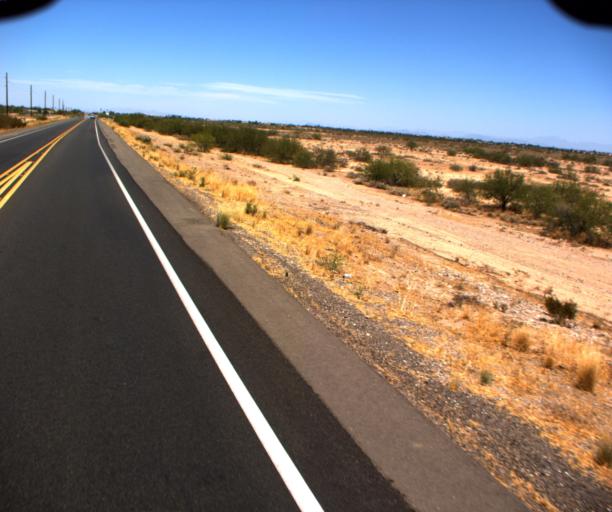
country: US
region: Arizona
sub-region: Maricopa County
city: Sun Lakes
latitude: 33.1887
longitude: -111.8409
